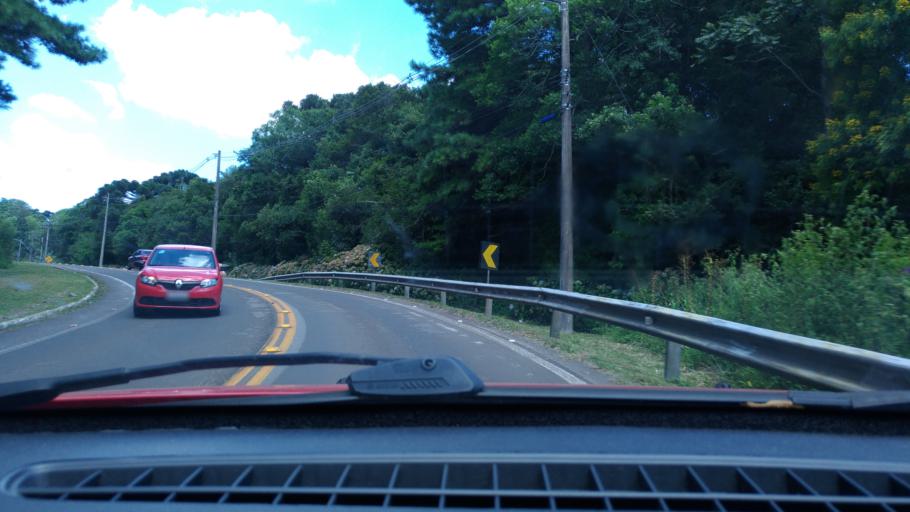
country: BR
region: Rio Grande do Sul
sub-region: Canela
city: Canela
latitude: -29.3531
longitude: -50.8330
